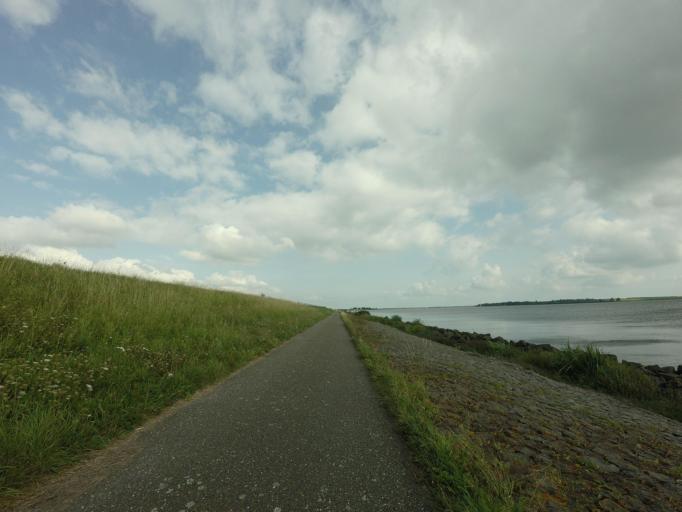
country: NL
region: Flevoland
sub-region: Gemeente Dronten
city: Dronten
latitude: 52.6130
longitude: 5.7200
